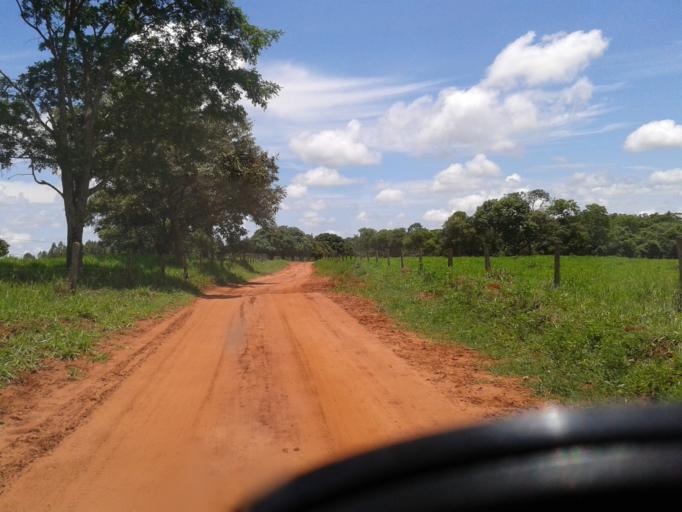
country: BR
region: Minas Gerais
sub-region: Santa Vitoria
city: Santa Vitoria
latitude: -18.9740
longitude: -49.8882
